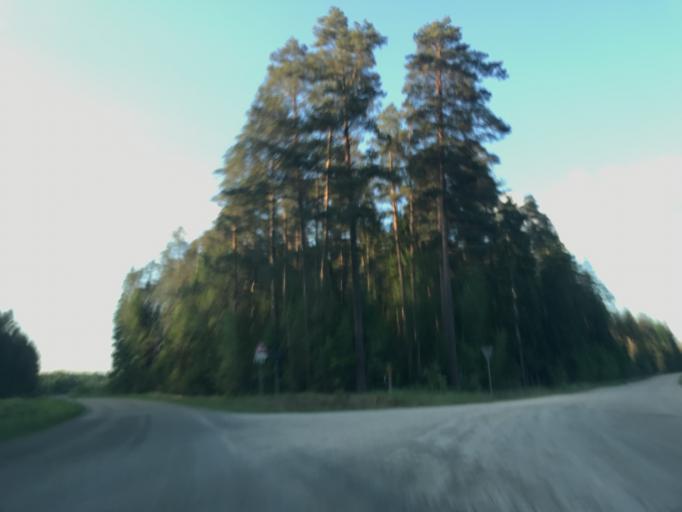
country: LV
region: Lecava
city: Iecava
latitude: 56.6524
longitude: 24.3002
